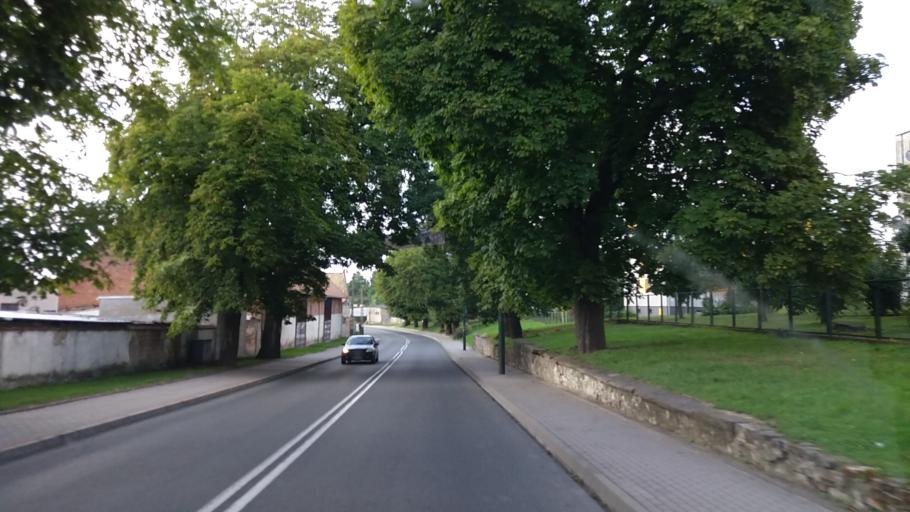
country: PL
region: West Pomeranian Voivodeship
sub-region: Powiat choszczenski
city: Pelczyce
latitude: 53.0456
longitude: 15.3018
